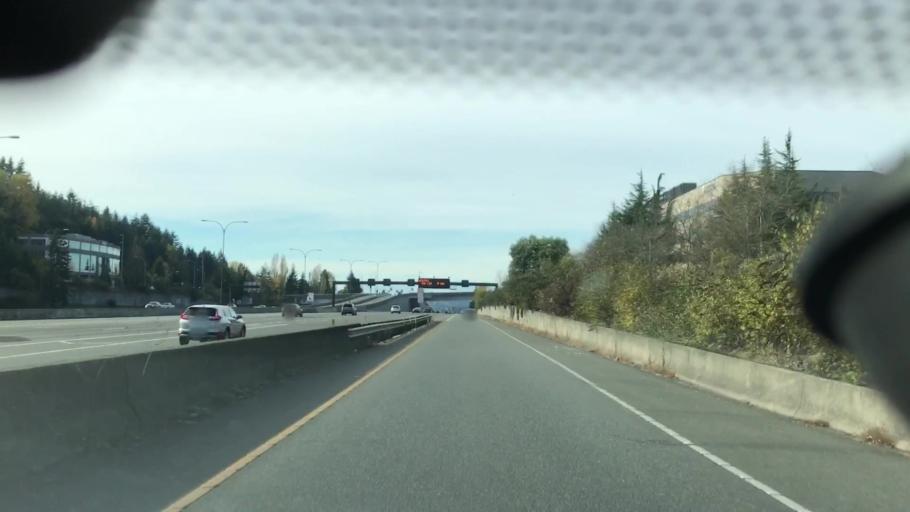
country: US
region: Washington
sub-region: King County
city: Eastgate
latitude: 47.5796
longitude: -122.1446
